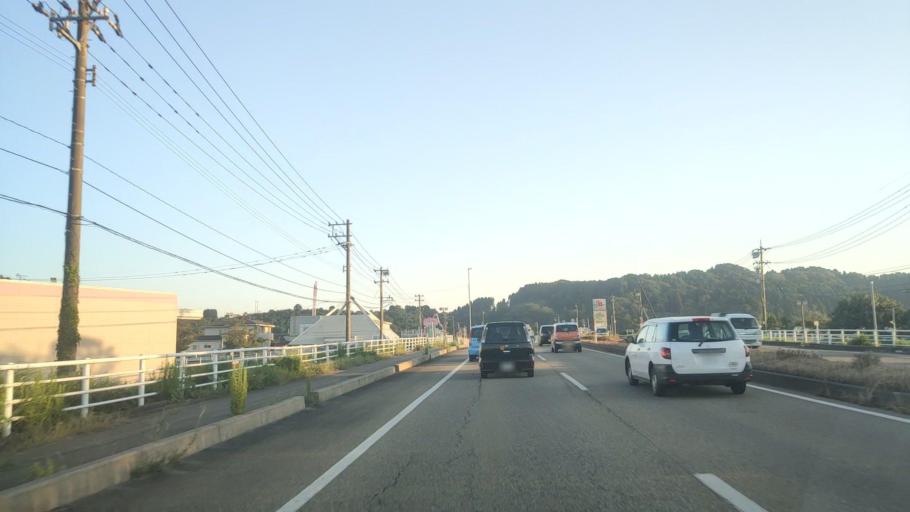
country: JP
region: Toyama
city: Himi
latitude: 36.8623
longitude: 136.9757
